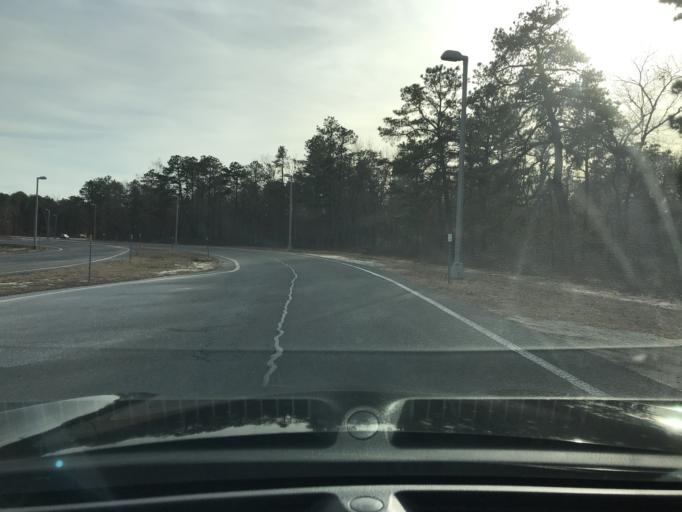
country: US
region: New Jersey
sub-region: Ocean County
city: Waretown
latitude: 39.7947
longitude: -74.2395
